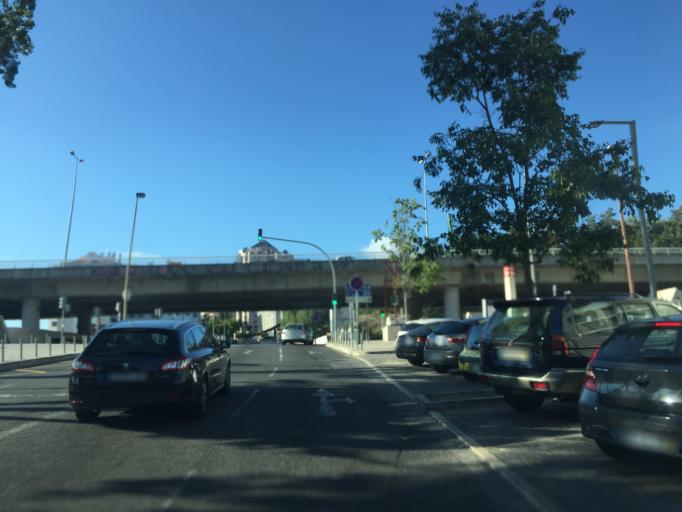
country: PT
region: Lisbon
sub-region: Odivelas
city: Pontinha
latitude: 38.7493
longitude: -9.1801
